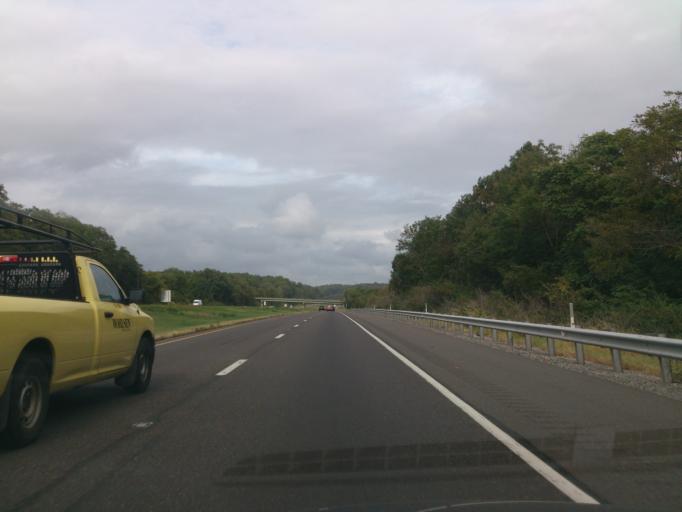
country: US
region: Pennsylvania
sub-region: Lancaster County
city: Ephrata
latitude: 40.1733
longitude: -76.1452
